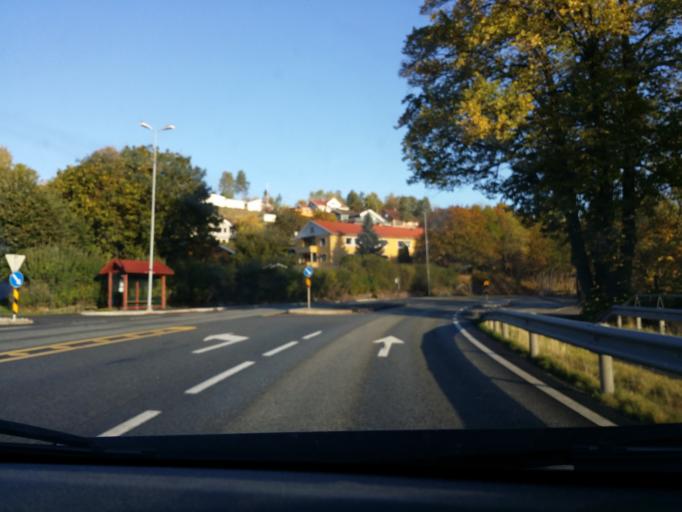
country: NO
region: Buskerud
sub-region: Hole
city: Vik
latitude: 60.0654
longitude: 10.2984
